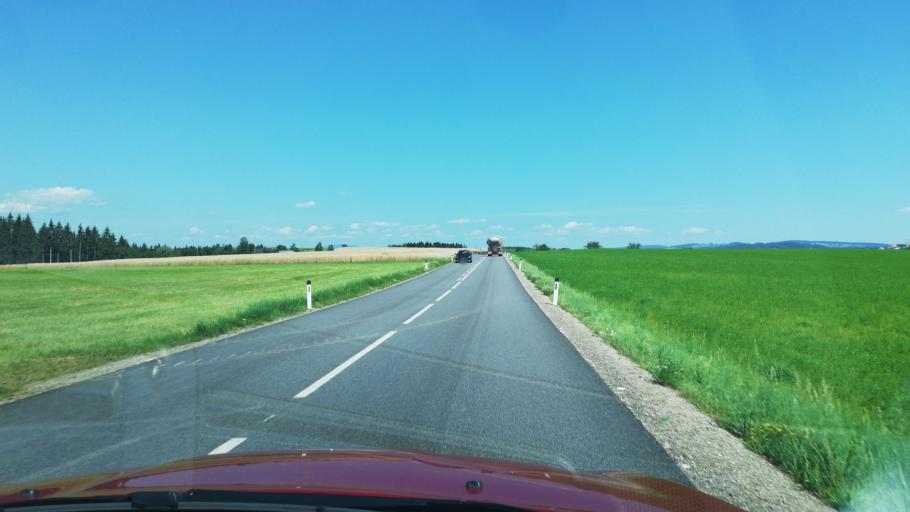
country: AT
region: Upper Austria
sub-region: Politischer Bezirk Urfahr-Umgebung
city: Herzogsdorf
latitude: 48.4718
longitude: 14.0613
